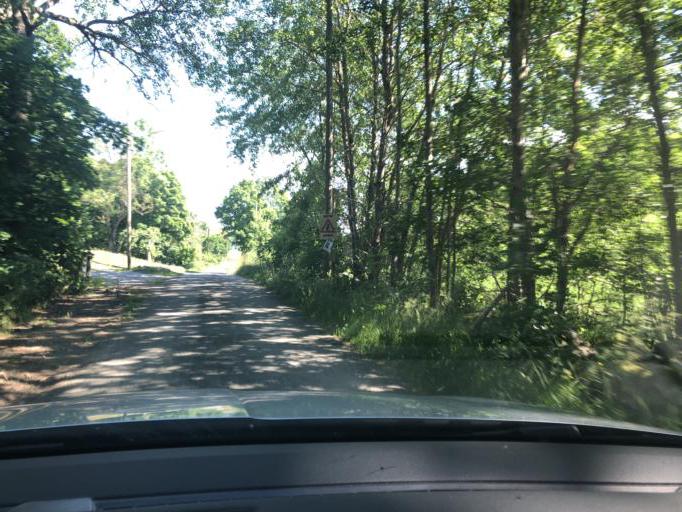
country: SE
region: Blekinge
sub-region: Karlshamns Kommun
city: Morrum
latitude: 56.1885
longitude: 14.6987
